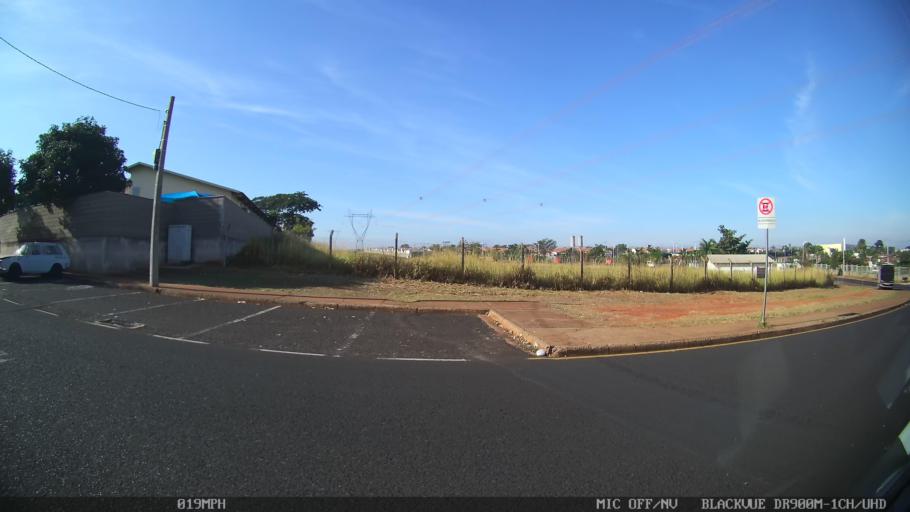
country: BR
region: Sao Paulo
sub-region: Sao Jose Do Rio Preto
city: Sao Jose do Rio Preto
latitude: -20.7685
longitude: -49.3305
